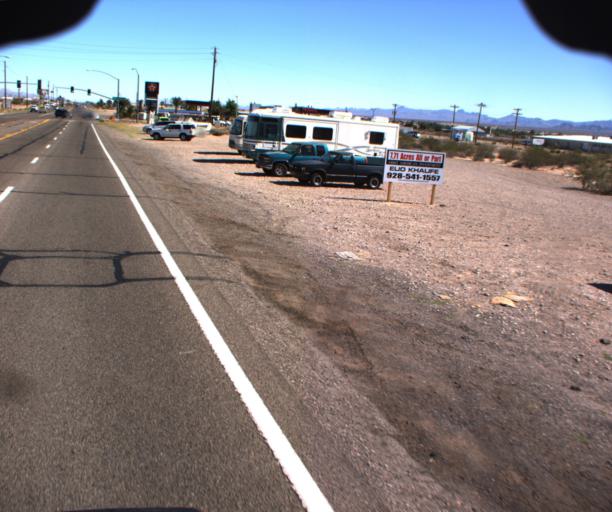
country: US
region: Arizona
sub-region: Mohave County
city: Mohave Valley
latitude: 34.9957
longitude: -114.5979
